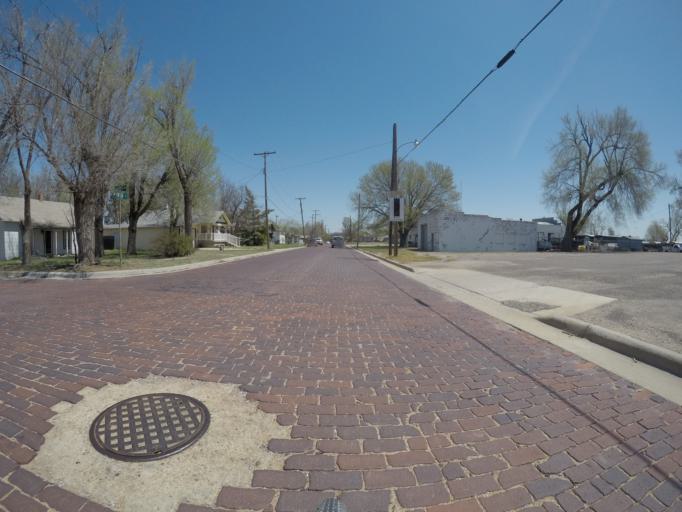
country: US
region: Kansas
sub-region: Pratt County
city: Pratt
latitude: 37.6421
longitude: -98.7521
